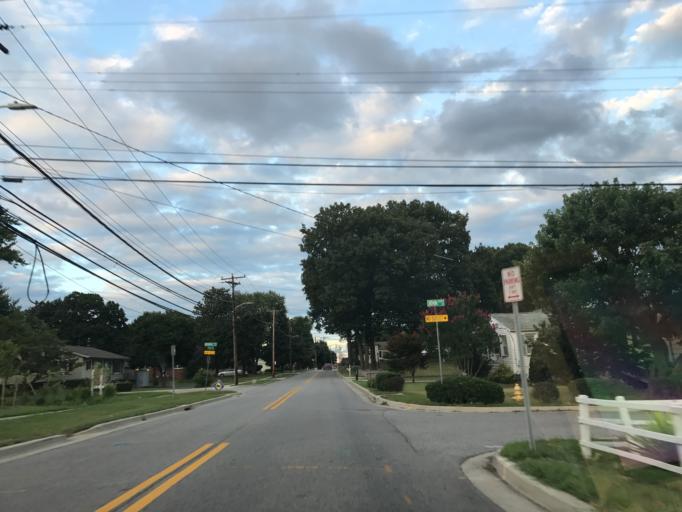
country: US
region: Maryland
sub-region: Anne Arundel County
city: Ferndale
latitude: 39.1867
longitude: -76.6235
